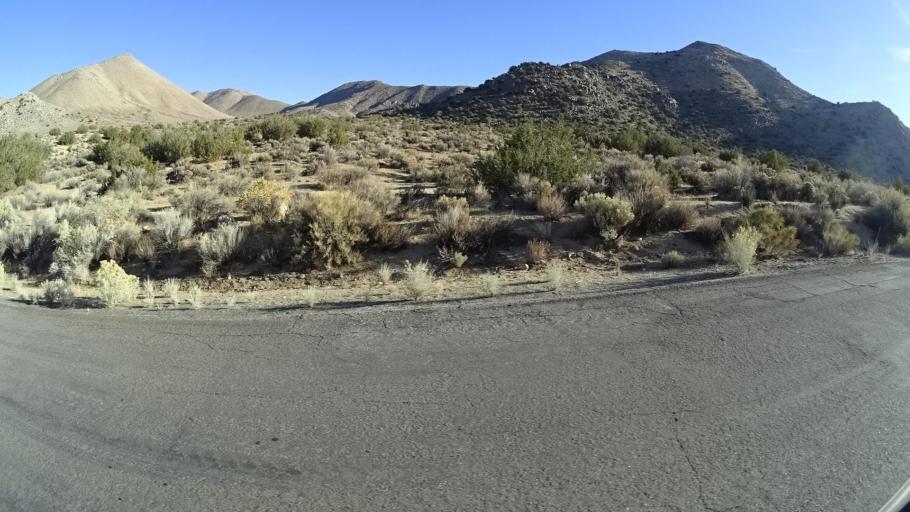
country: US
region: California
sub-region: Kern County
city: Weldon
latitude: 35.5856
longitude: -118.2451
